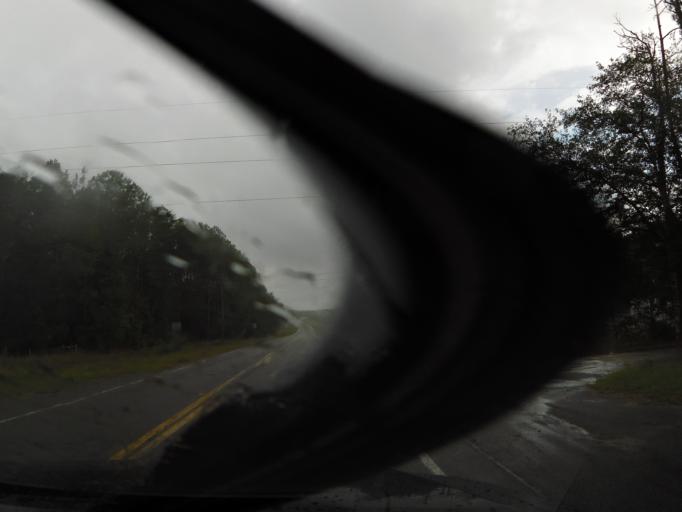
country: US
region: Florida
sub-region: Nassau County
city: Callahan
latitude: 30.5235
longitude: -82.0272
